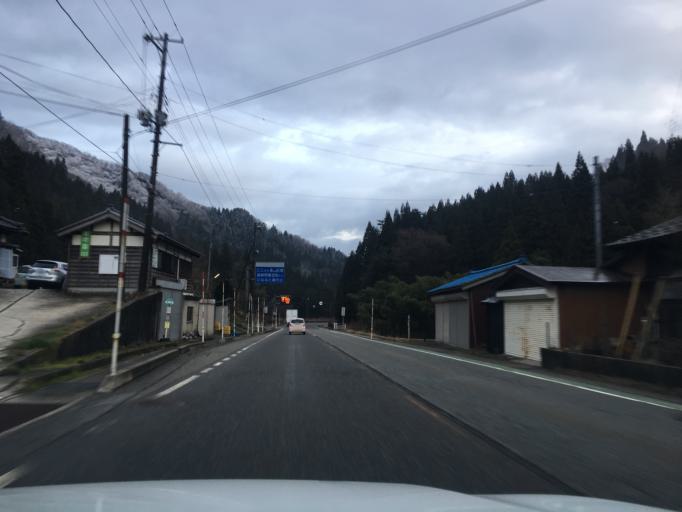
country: JP
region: Niigata
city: Murakami
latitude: 38.3901
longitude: 139.5551
